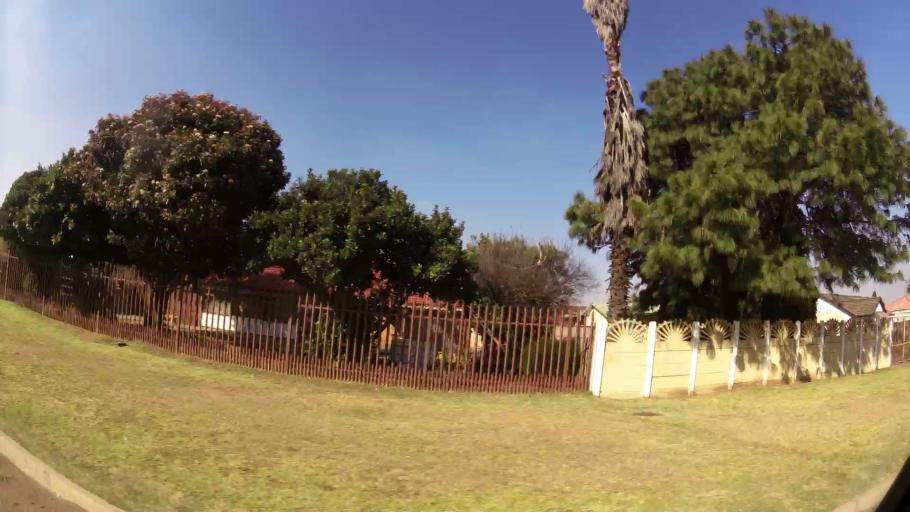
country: ZA
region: Gauteng
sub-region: Ekurhuleni Metropolitan Municipality
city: Boksburg
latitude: -26.2443
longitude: 28.2945
